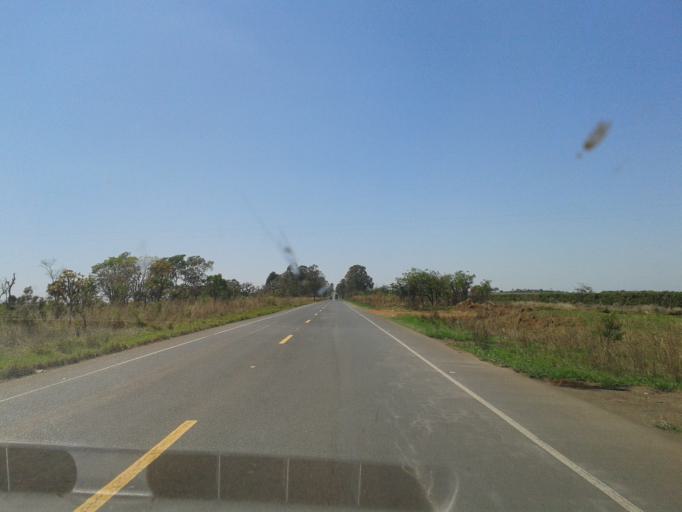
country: BR
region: Minas Gerais
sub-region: Araxa
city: Araxa
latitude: -19.4207
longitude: -47.2723
